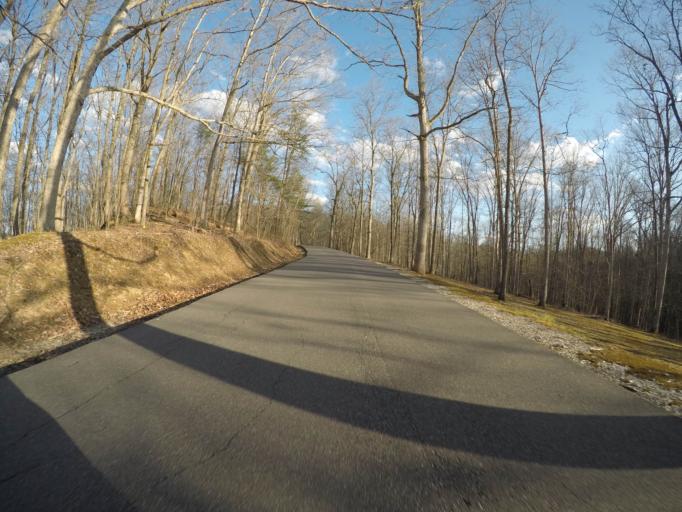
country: US
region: West Virginia
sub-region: Kanawha County
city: Charleston
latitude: 38.3924
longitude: -81.5706
